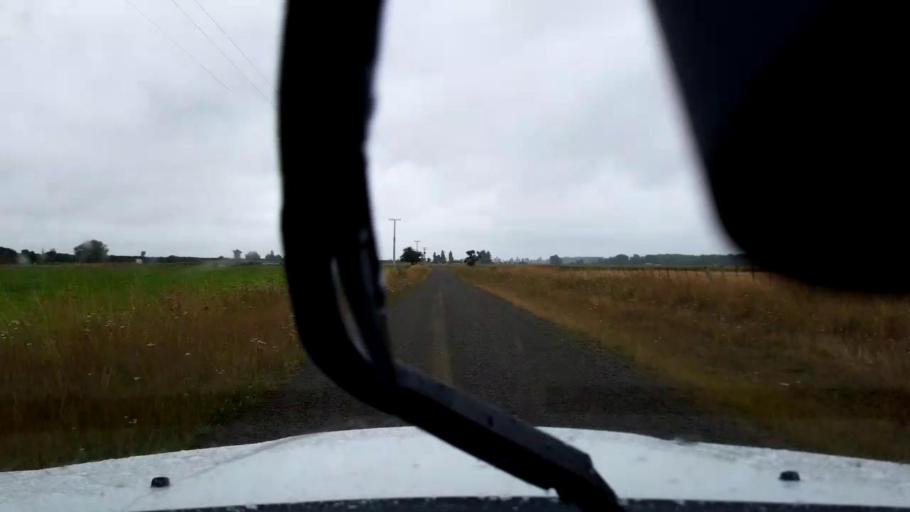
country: NZ
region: Canterbury
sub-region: Timaru District
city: Pleasant Point
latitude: -44.2534
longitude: 171.2035
